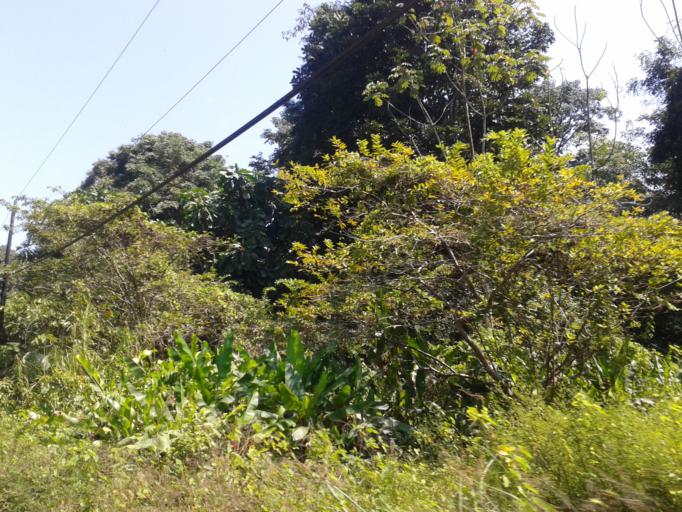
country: CR
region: Limon
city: Sixaola
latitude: 9.6282
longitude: -82.6613
